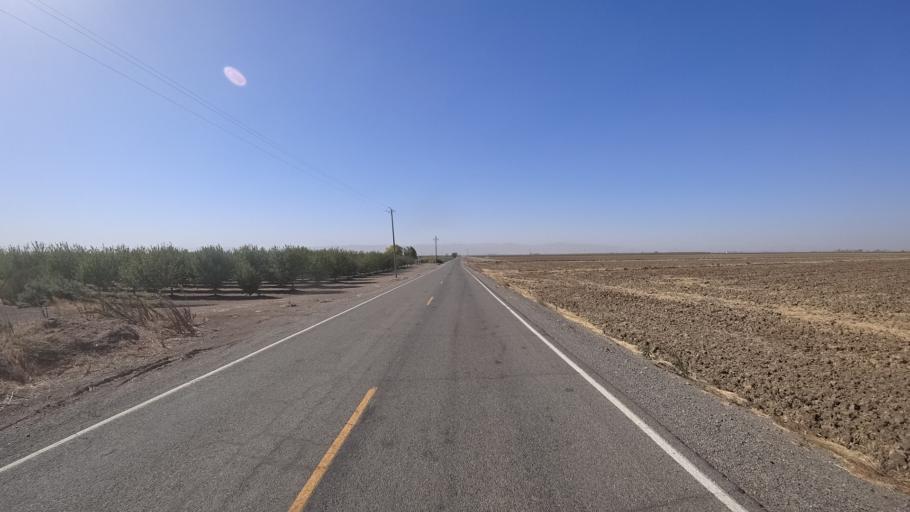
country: US
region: California
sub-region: Yolo County
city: Winters
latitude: 38.5907
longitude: -121.8936
